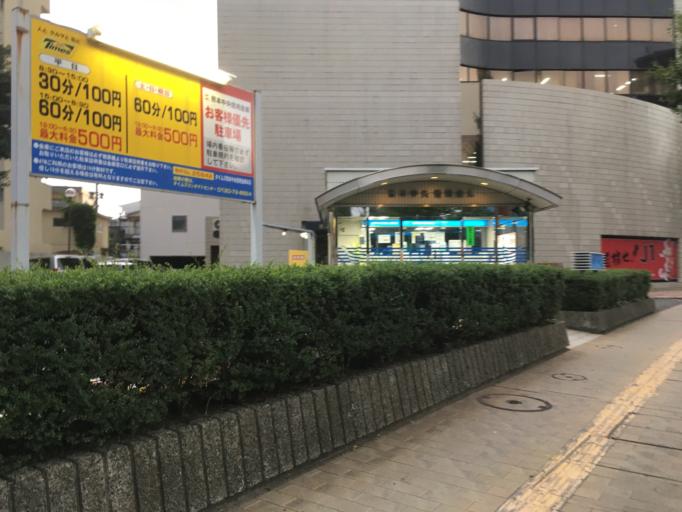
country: JP
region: Kumamoto
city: Kumamoto
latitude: 32.7967
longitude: 130.7209
